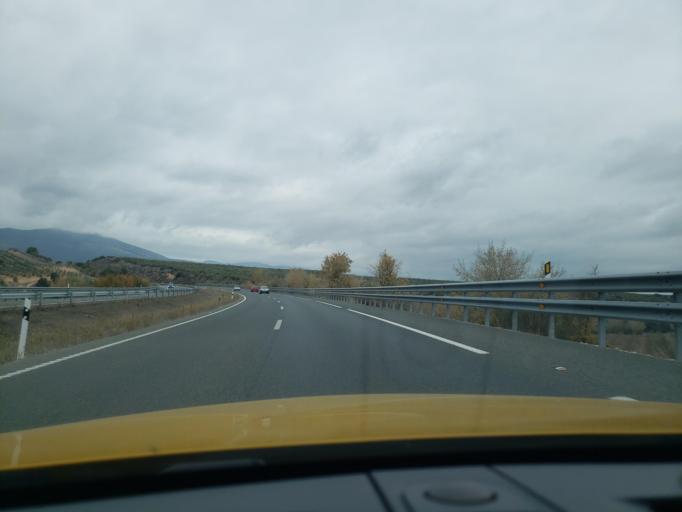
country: ES
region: Andalusia
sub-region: Provincia de Granada
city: Calicasas
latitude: 37.2923
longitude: -3.6566
